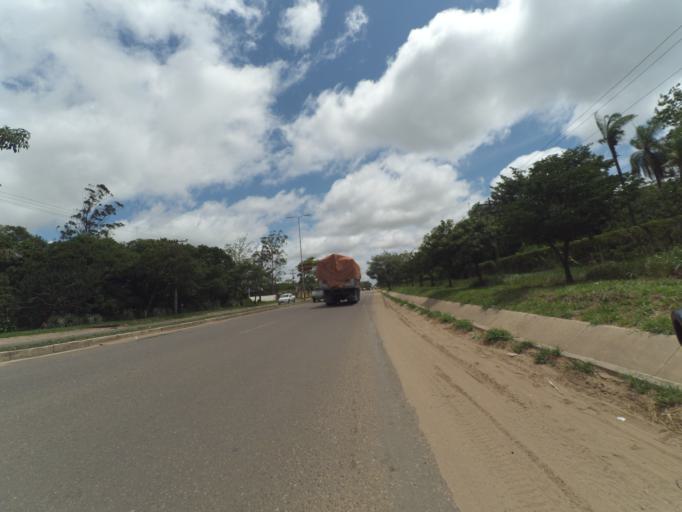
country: BO
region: Santa Cruz
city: Santa Cruz de la Sierra
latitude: -17.8693
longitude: -63.2731
